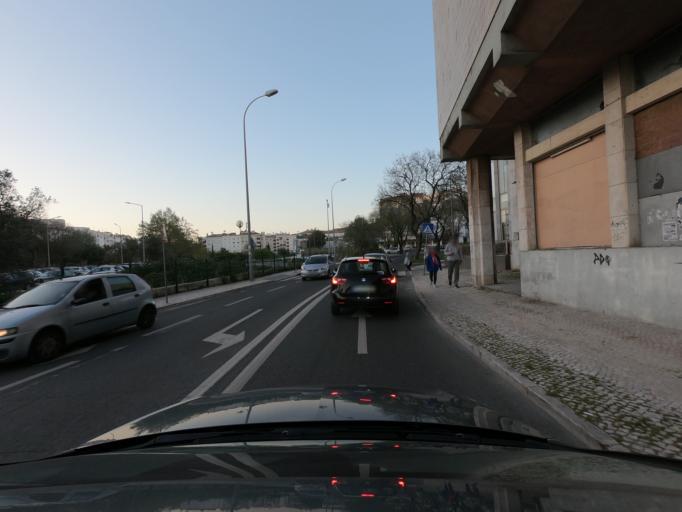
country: PT
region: Lisbon
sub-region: Sintra
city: Queluz
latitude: 38.7567
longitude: -9.2482
